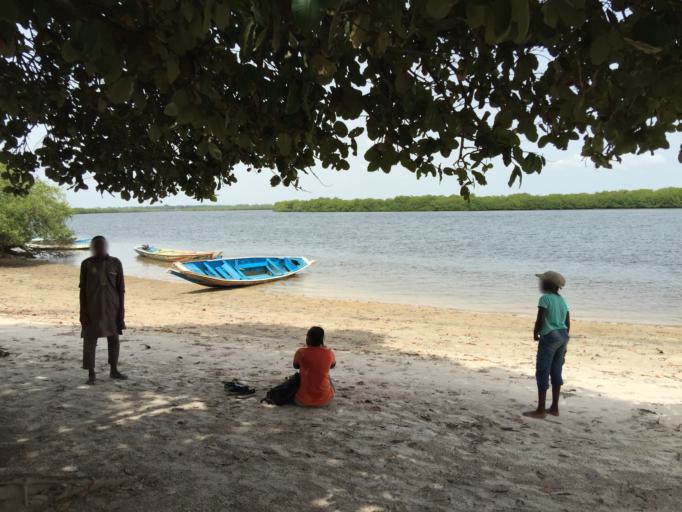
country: SN
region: Fatick
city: Sokone
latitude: 13.7500
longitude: -16.5091
